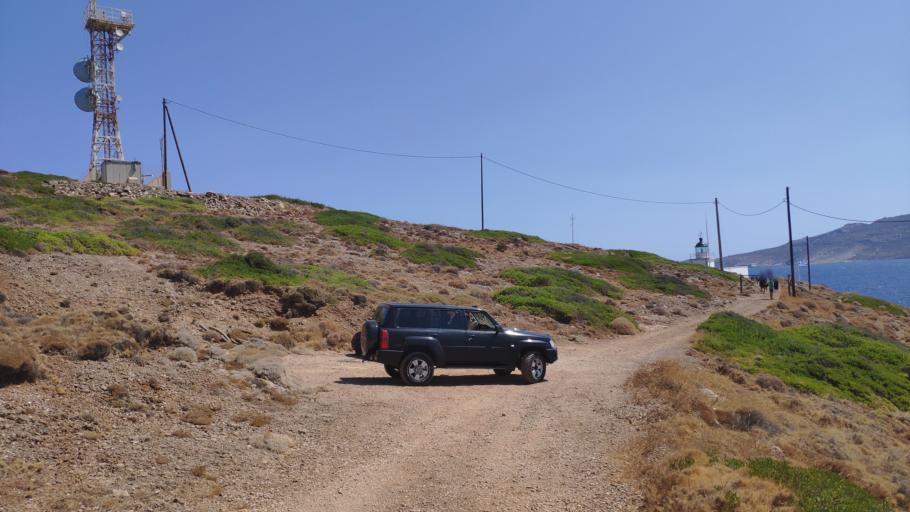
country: GR
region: Attica
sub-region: Nomarchia Anatolikis Attikis
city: Lavrio
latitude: 37.7442
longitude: 24.0795
